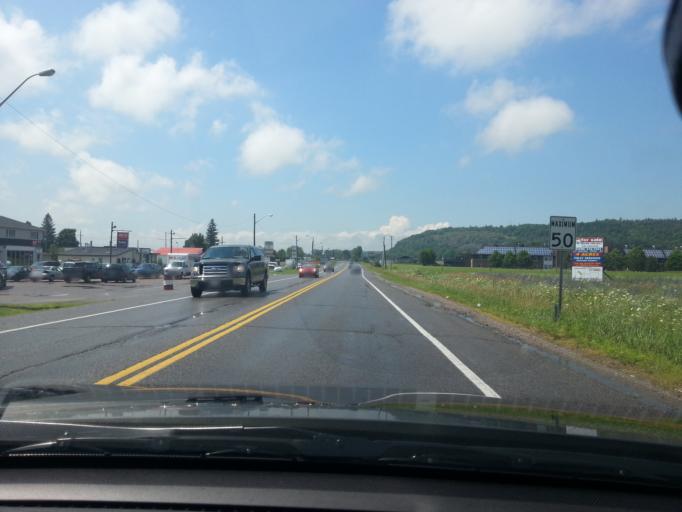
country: CA
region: Ontario
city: Renfrew
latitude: 45.4807
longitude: -76.7002
